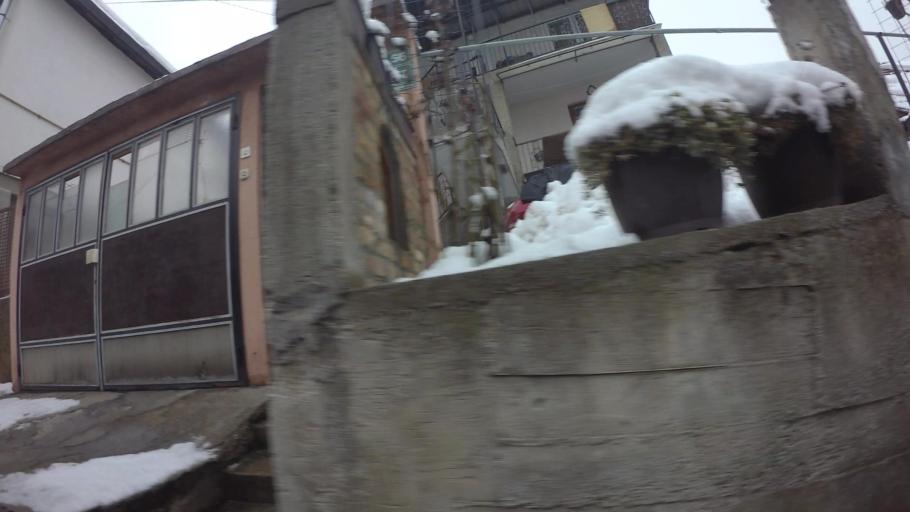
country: BA
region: Federation of Bosnia and Herzegovina
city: Kobilja Glava
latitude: 43.8497
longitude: 18.4259
